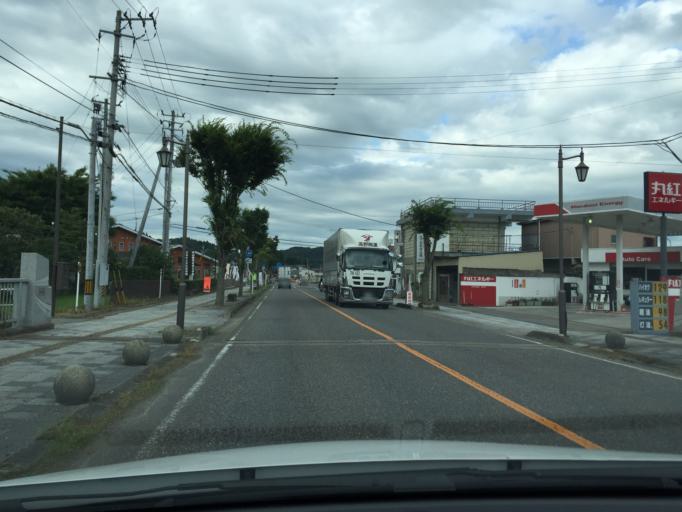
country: JP
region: Fukushima
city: Sukagawa
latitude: 37.2024
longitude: 140.2477
